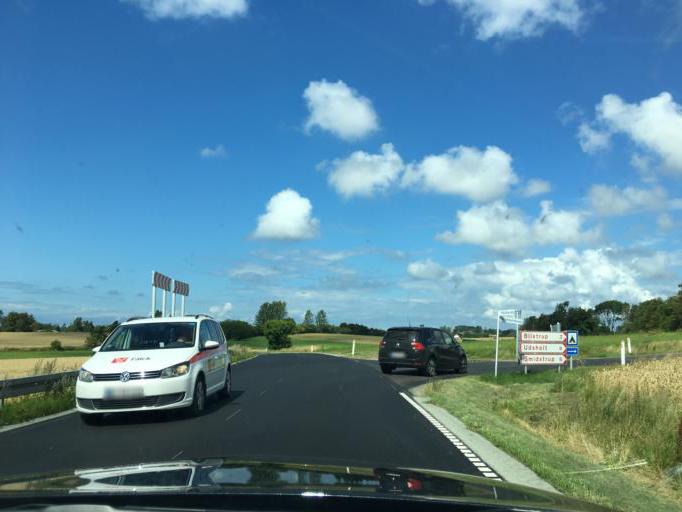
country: DK
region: Capital Region
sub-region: Gribskov Kommune
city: Helsinge
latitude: 56.0648
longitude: 12.2026
